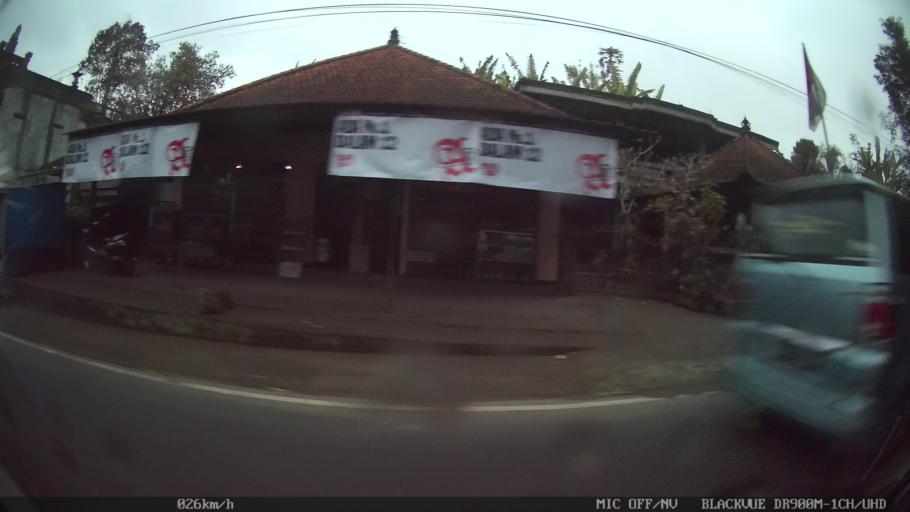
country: ID
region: Bali
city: Banjar Buahan
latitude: -8.4036
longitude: 115.2470
